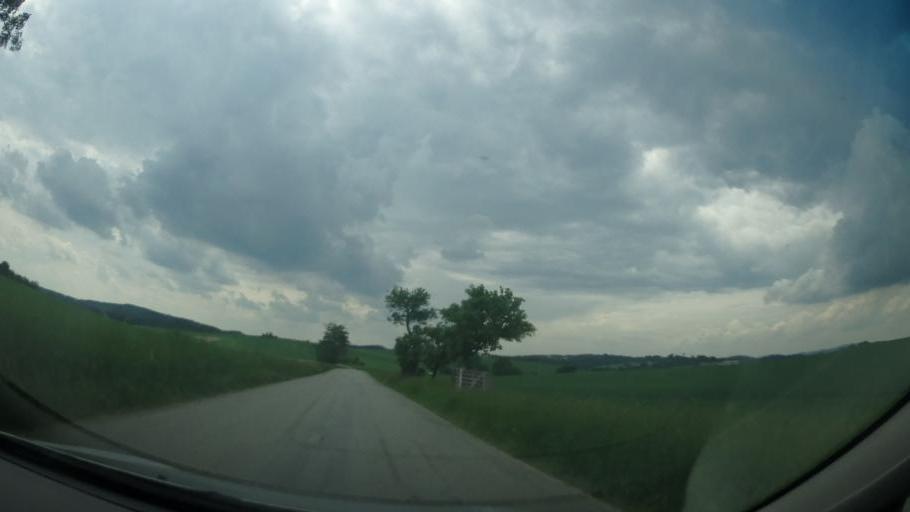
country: CZ
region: South Moravian
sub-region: Okres Brno-Venkov
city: Lomnice
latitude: 49.4783
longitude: 16.4341
